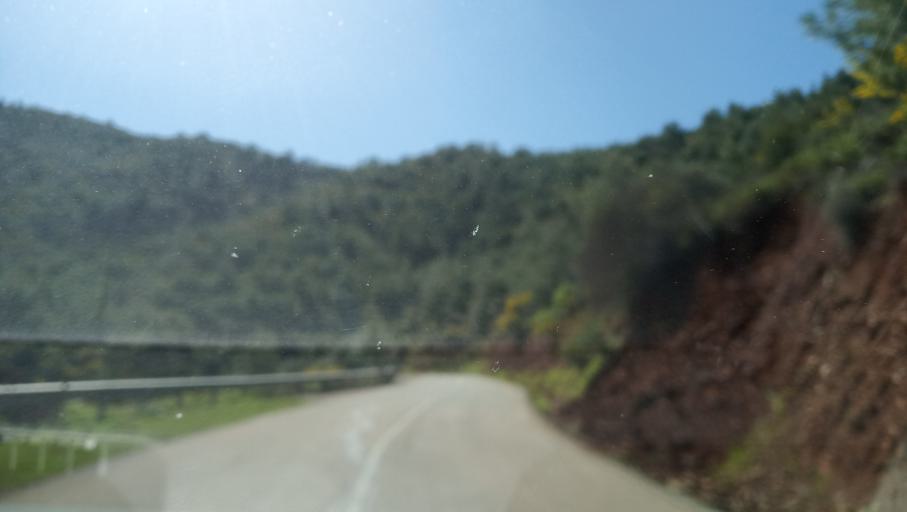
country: CY
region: Lefkosia
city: Lefka
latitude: 35.0730
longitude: 32.8109
